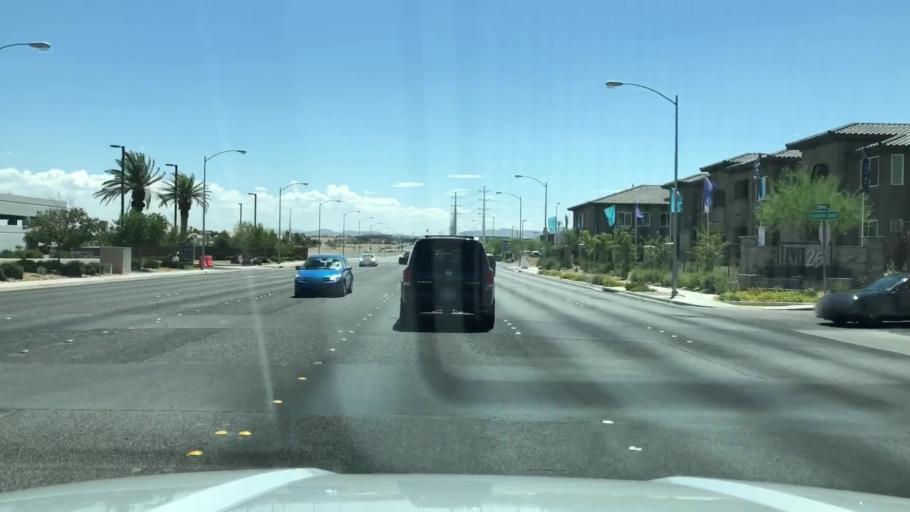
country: US
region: Nevada
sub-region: Clark County
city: Spring Valley
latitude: 36.0900
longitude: -115.2793
